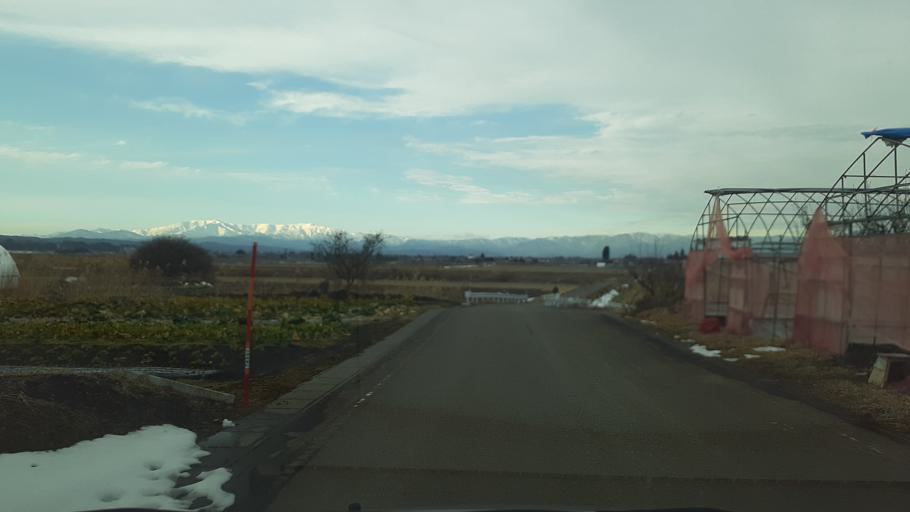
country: JP
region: Fukushima
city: Kitakata
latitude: 37.4710
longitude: 139.8473
